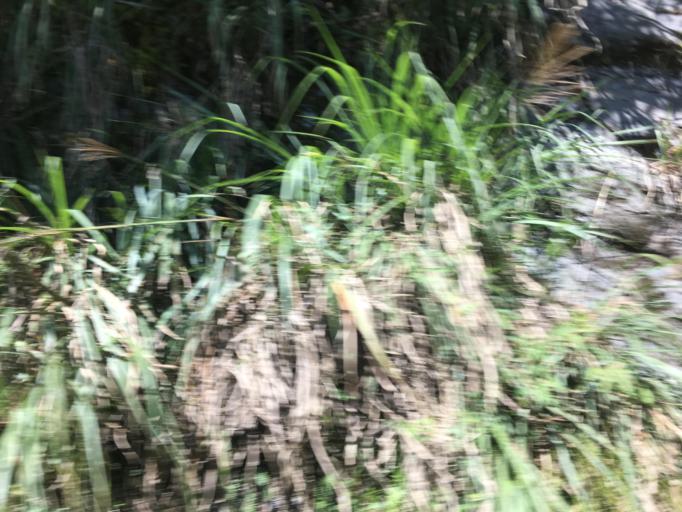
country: TW
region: Taiwan
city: Daxi
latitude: 24.6097
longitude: 121.4592
